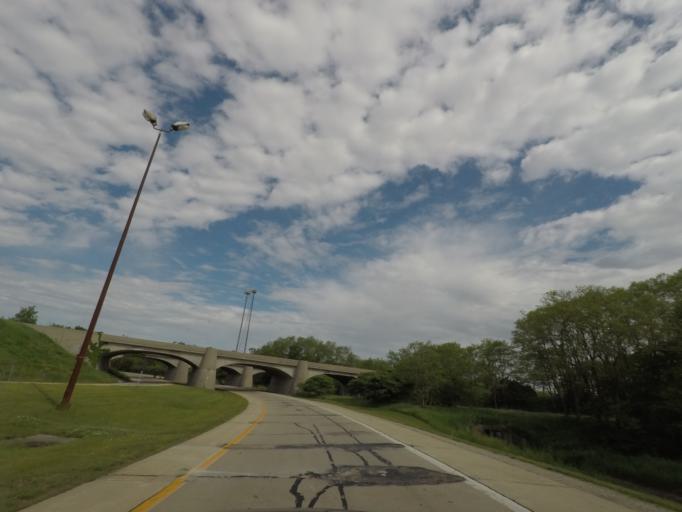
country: US
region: Illinois
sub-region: McLean County
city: Twin Grove
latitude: 40.3623
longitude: -89.1044
